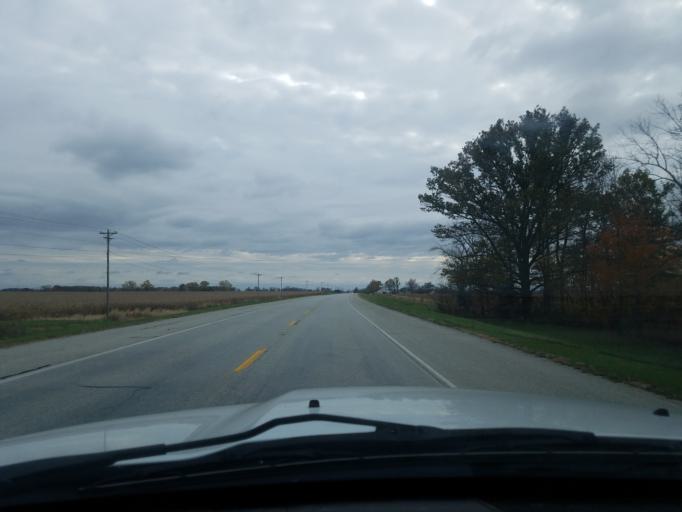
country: US
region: Indiana
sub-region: Bartholomew County
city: Hope
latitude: 39.2111
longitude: -85.7718
